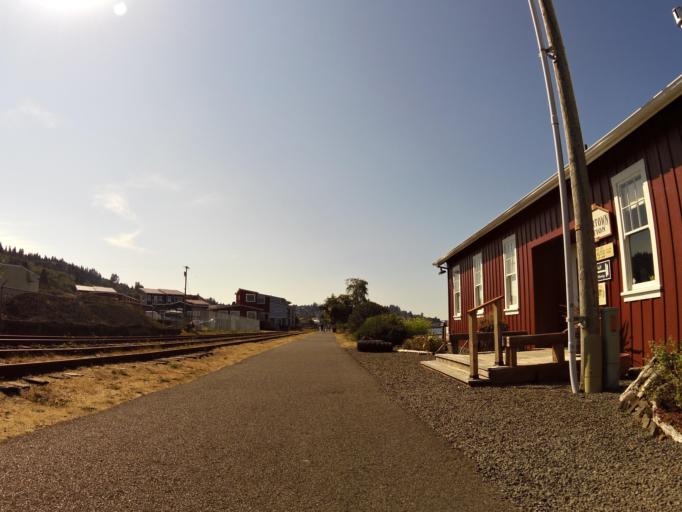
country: US
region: Oregon
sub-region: Clatsop County
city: Astoria
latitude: 46.1923
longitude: -123.8109
